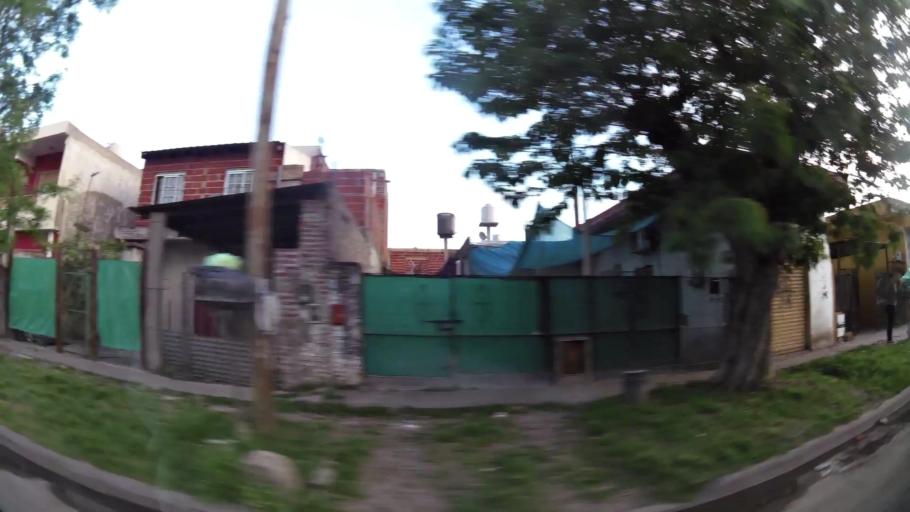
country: AR
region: Buenos Aires
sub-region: Partido de Quilmes
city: Quilmes
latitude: -34.8008
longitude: -58.2904
